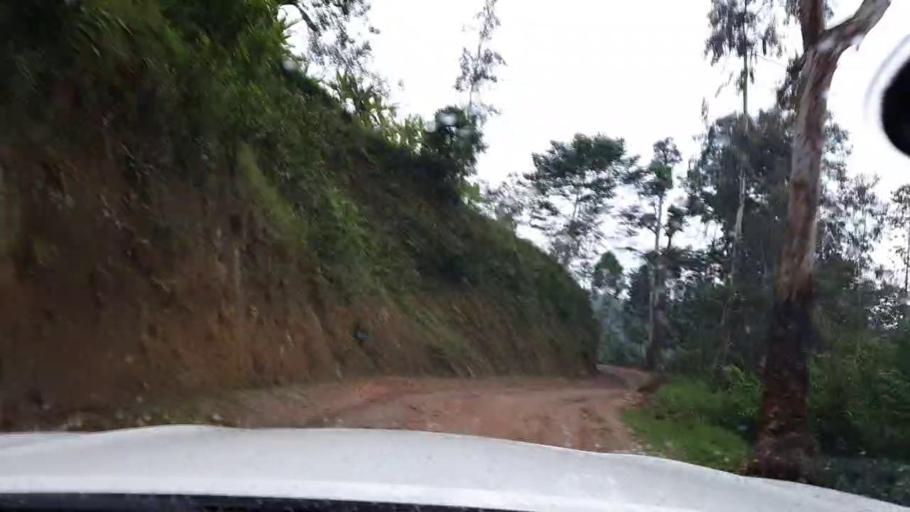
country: RW
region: Western Province
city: Cyangugu
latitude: -2.4105
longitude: 29.1889
